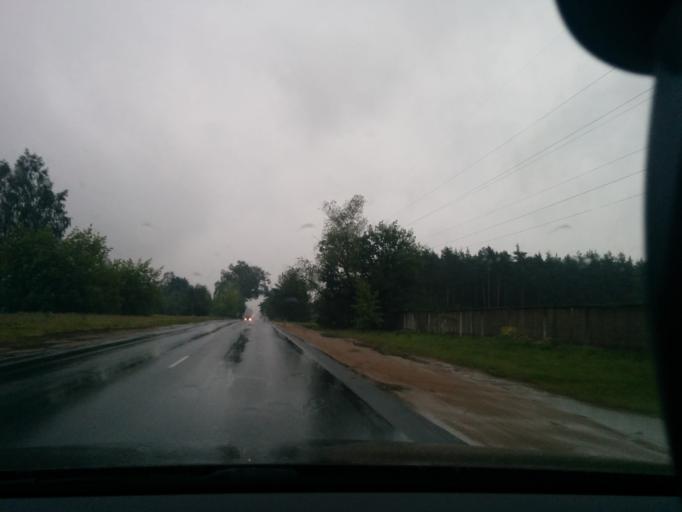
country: LV
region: Stopini
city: Ulbroka
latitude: 56.9128
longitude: 24.2315
